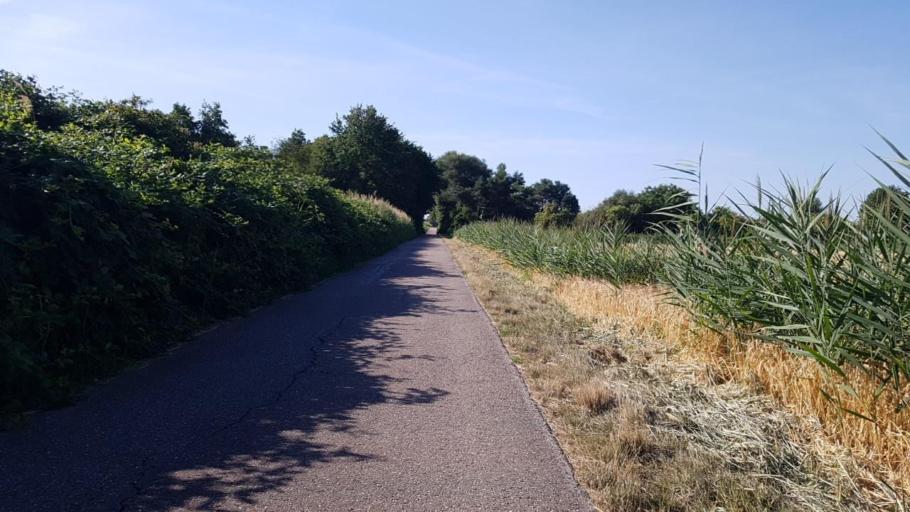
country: DE
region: Baden-Wuerttemberg
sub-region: Karlsruhe Region
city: Sankt Leon-Rot
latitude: 49.2817
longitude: 8.6133
